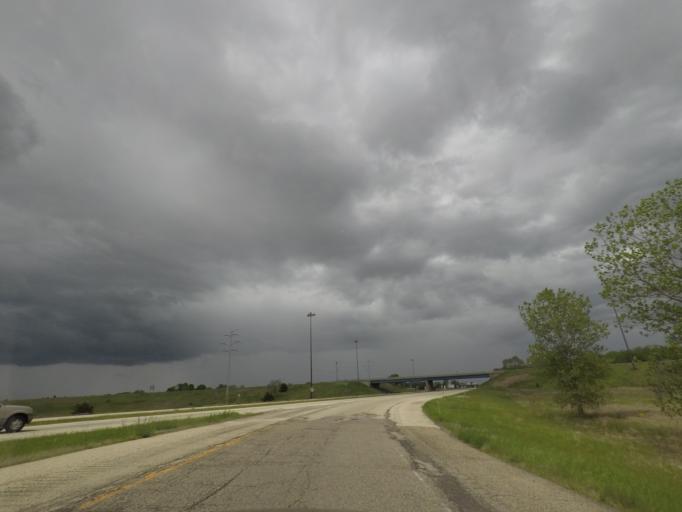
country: US
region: Illinois
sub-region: Winnebago County
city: Cherry Valley
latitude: 42.2205
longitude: -89.0088
